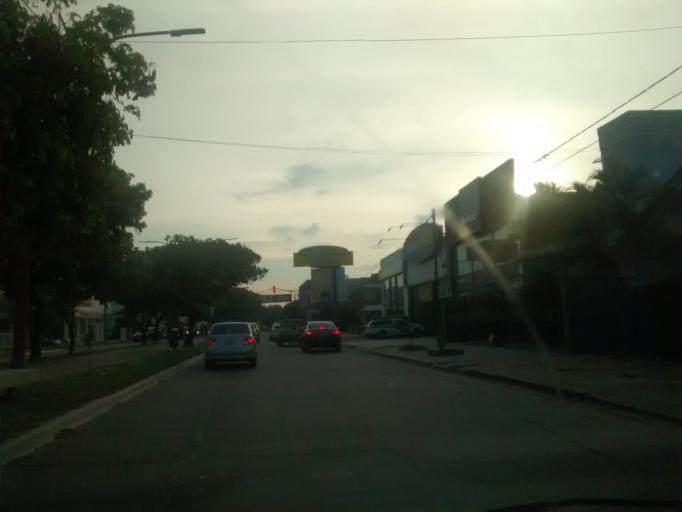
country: AR
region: Chaco
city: Resistencia
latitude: -27.4355
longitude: -58.9692
